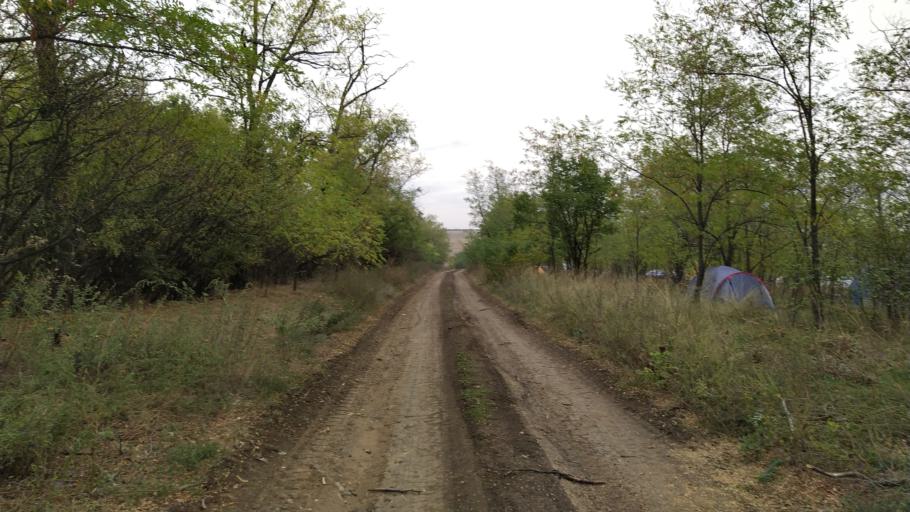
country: RU
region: Rostov
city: Gornyy
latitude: 47.8880
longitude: 40.2402
